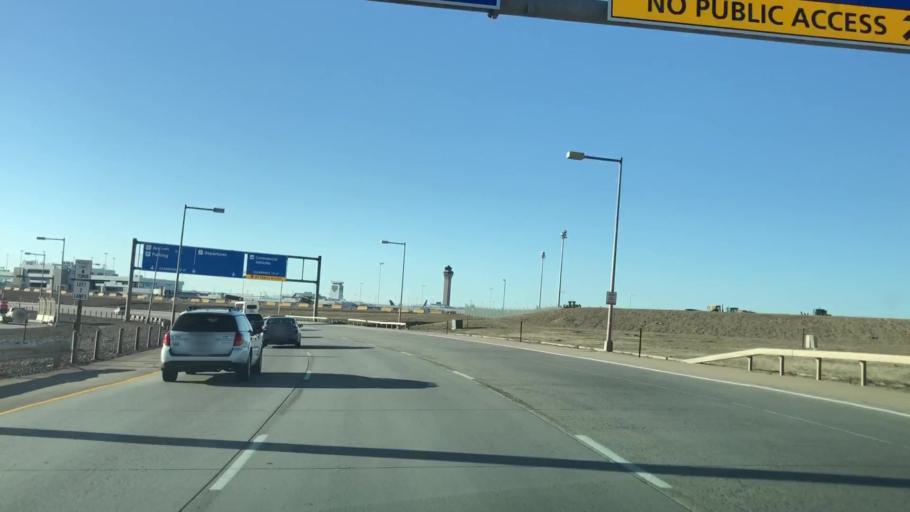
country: US
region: Colorado
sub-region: Weld County
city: Lochbuie
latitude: 39.8501
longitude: -104.6660
